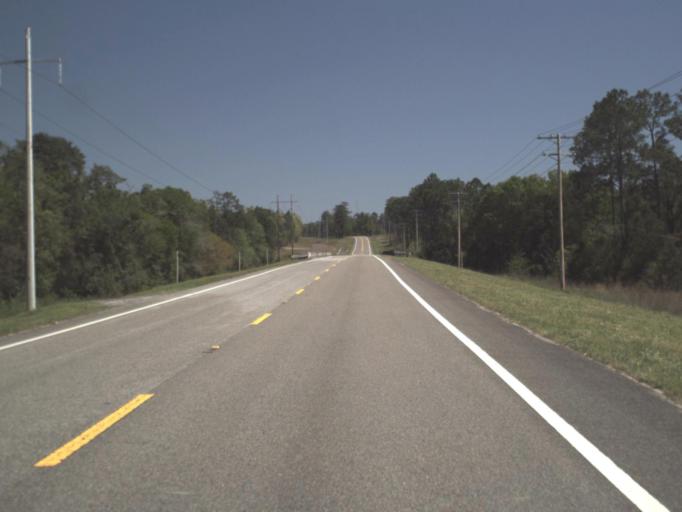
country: US
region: Florida
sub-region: Santa Rosa County
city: Point Baker
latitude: 30.8637
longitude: -86.9065
